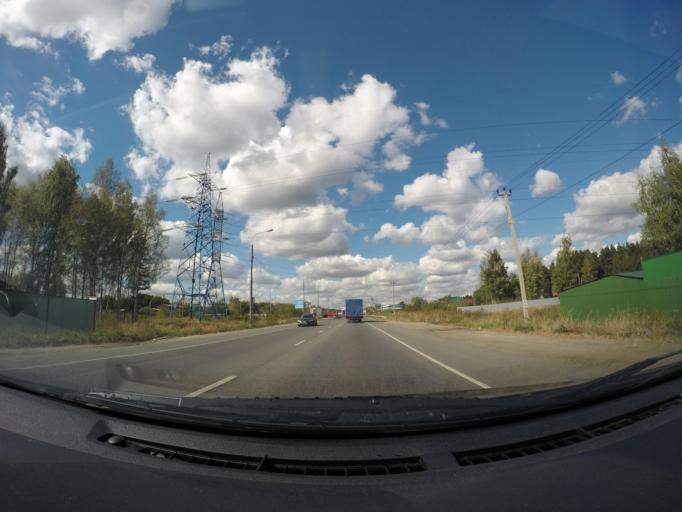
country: RU
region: Moskovskaya
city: Kratovo
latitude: 55.6407
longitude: 38.1645
